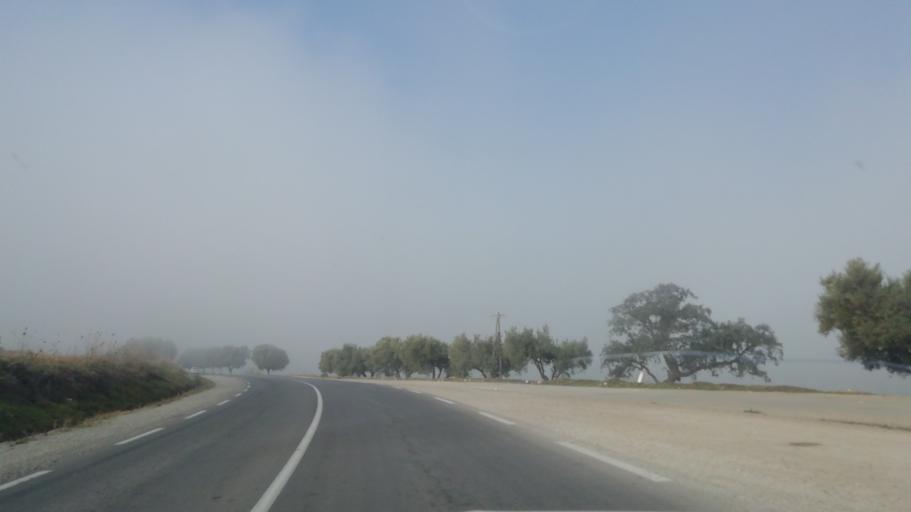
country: DZ
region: Mascara
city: Mascara
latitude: 35.5272
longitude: 0.3449
